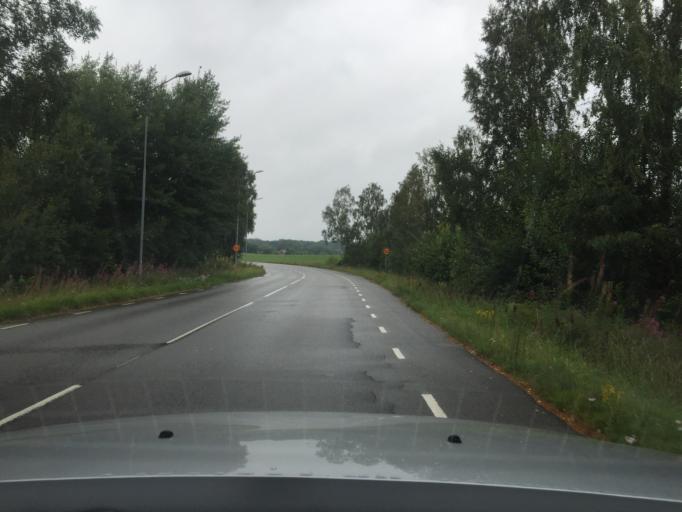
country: SE
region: Skane
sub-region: Hassleholms Kommun
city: Sosdala
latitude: 56.0074
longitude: 13.6477
